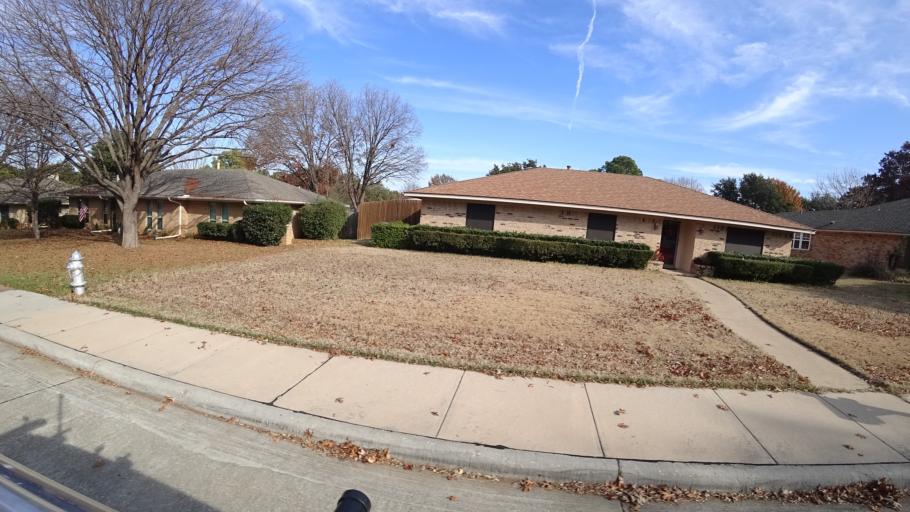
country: US
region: Texas
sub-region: Denton County
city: Lewisville
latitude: 33.0501
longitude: -97.0288
